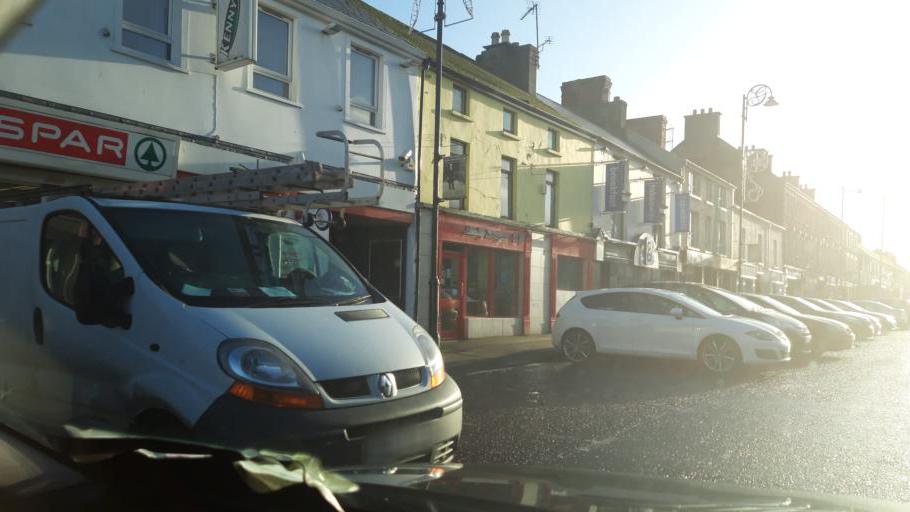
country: GB
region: Northern Ireland
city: Garvagh
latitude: 54.9831
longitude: -6.6875
